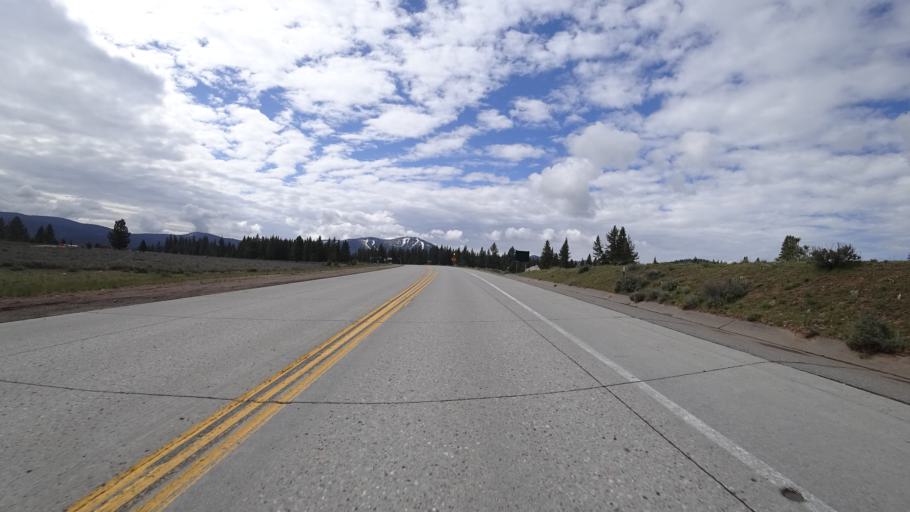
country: US
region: California
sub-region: Nevada County
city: Truckee
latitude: 39.3235
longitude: -120.1581
